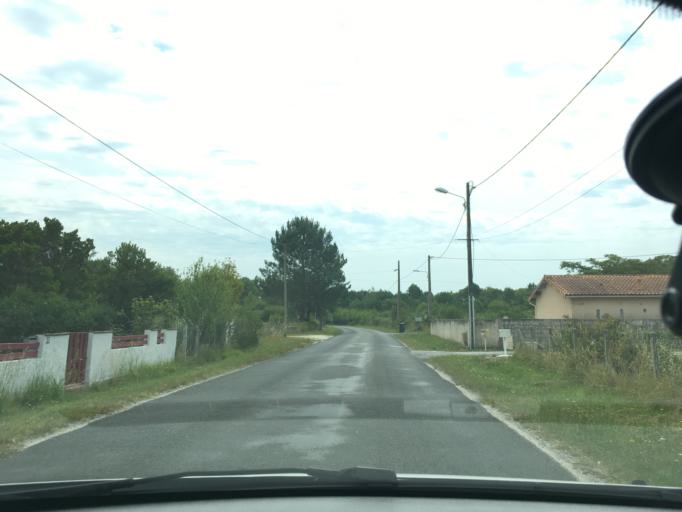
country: FR
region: Aquitaine
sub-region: Departement de la Gironde
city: Gaillan-en-Medoc
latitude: 45.3548
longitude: -1.0558
